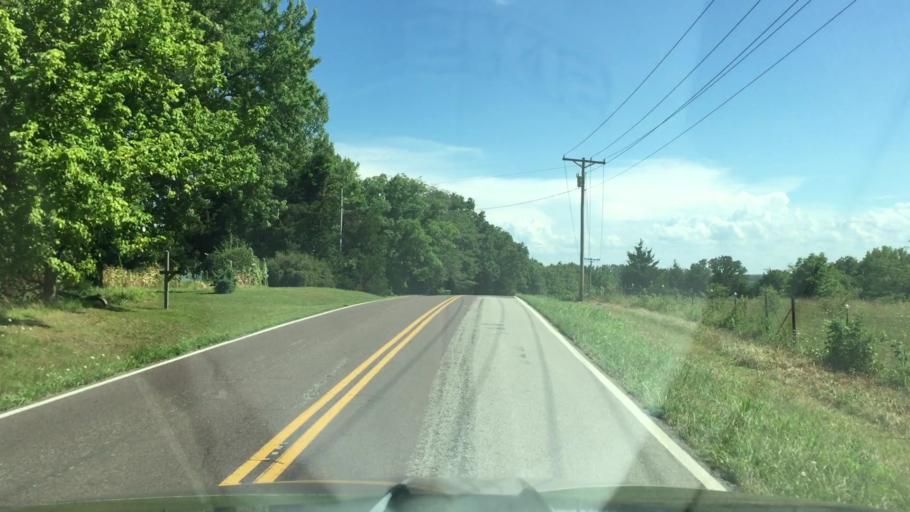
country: US
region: Missouri
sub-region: Miller County
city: Tuscumbia
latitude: 38.1077
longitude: -92.4731
